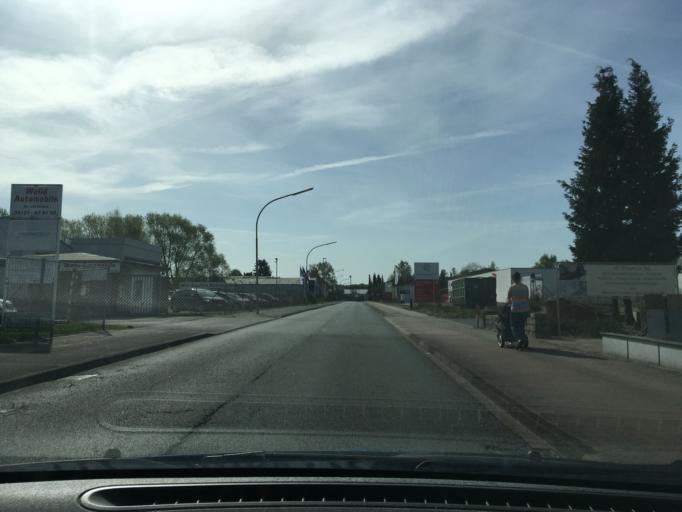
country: DE
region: Lower Saxony
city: Lueneburg
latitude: 53.2715
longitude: 10.4152
